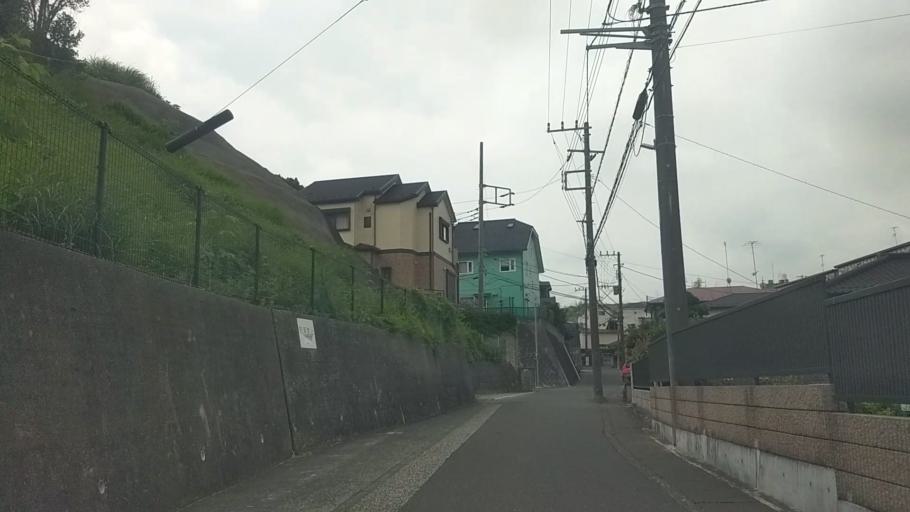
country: JP
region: Kanagawa
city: Kamakura
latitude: 35.3745
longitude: 139.5338
